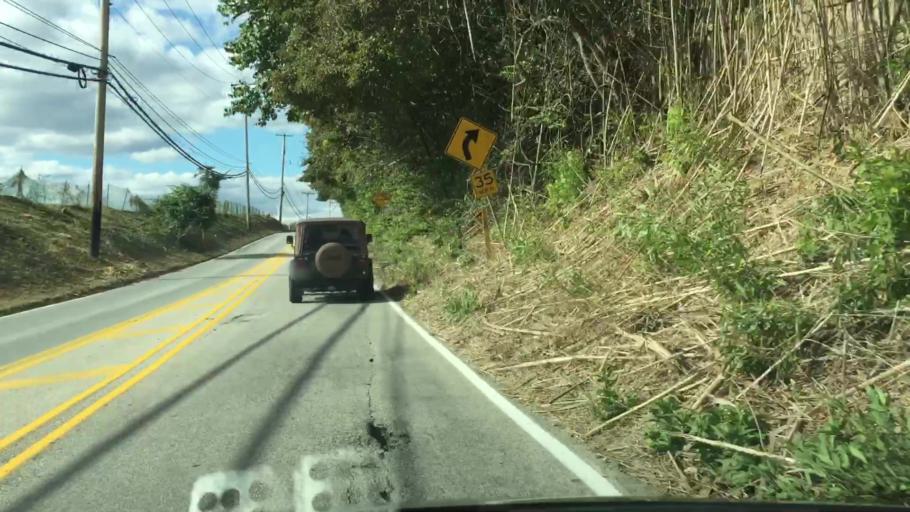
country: US
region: Pennsylvania
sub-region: Chester County
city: Malvern
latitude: 39.9899
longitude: -75.5535
